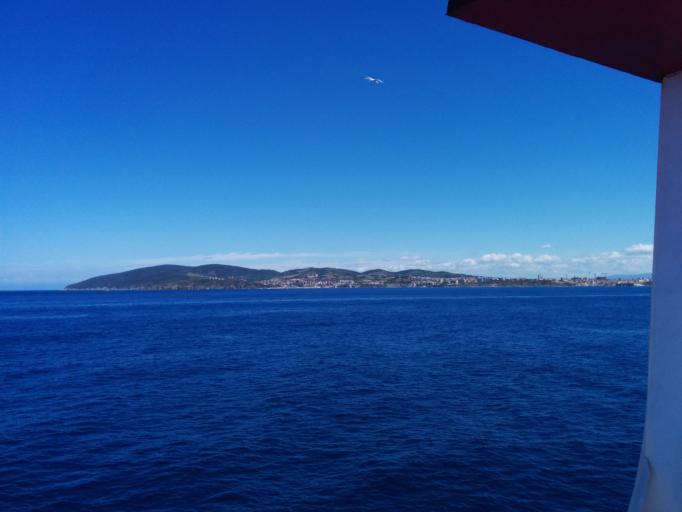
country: IT
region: Tuscany
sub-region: Provincia di Livorno
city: Piombino
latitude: 42.8974
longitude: 10.4965
